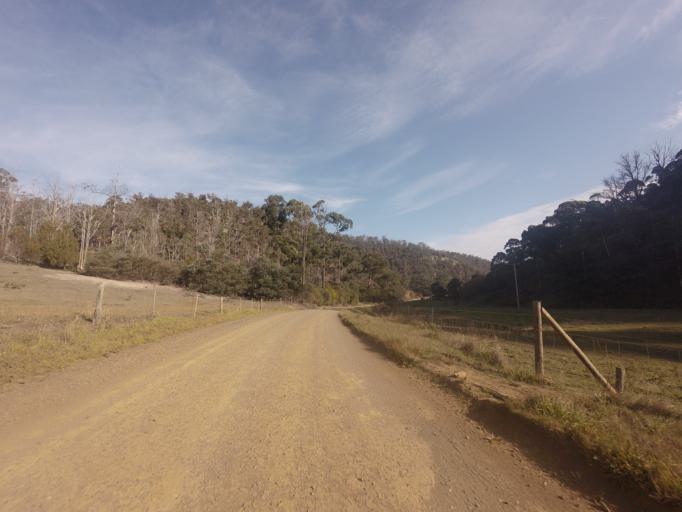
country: AU
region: Tasmania
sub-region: Brighton
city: Bridgewater
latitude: -42.5090
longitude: 147.4282
